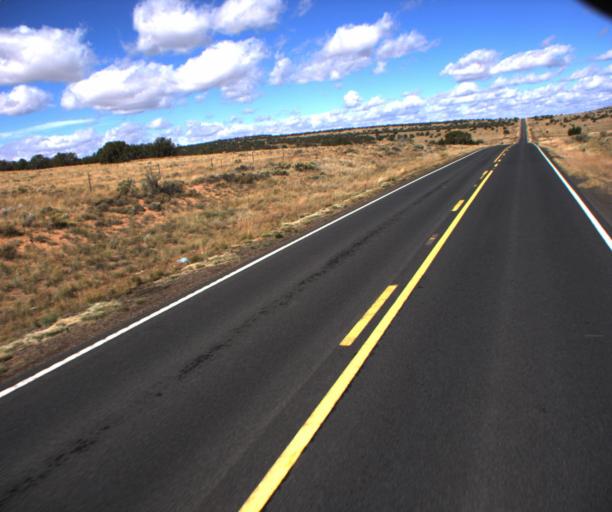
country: US
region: Arizona
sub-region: Apache County
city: Houck
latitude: 35.0105
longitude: -109.2328
